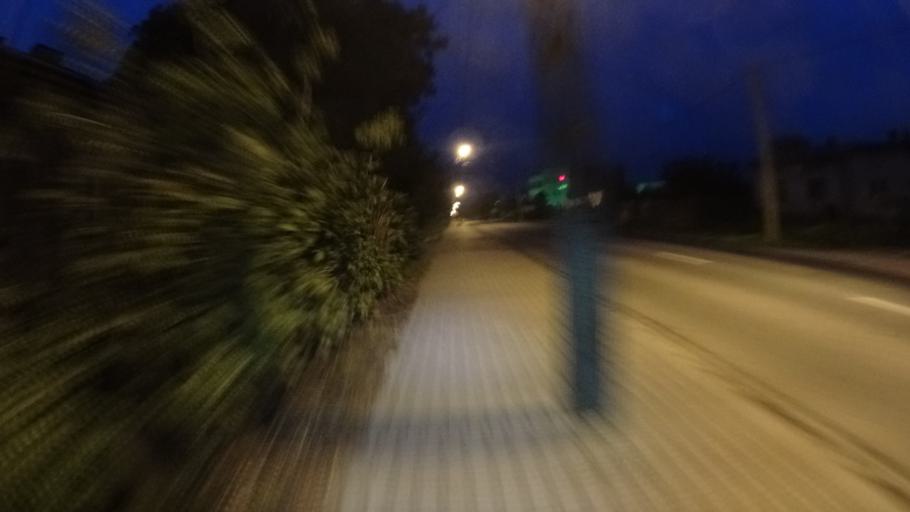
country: PL
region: Masovian Voivodeship
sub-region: Powiat warszawski zachodni
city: Babice
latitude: 52.2282
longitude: 20.8452
